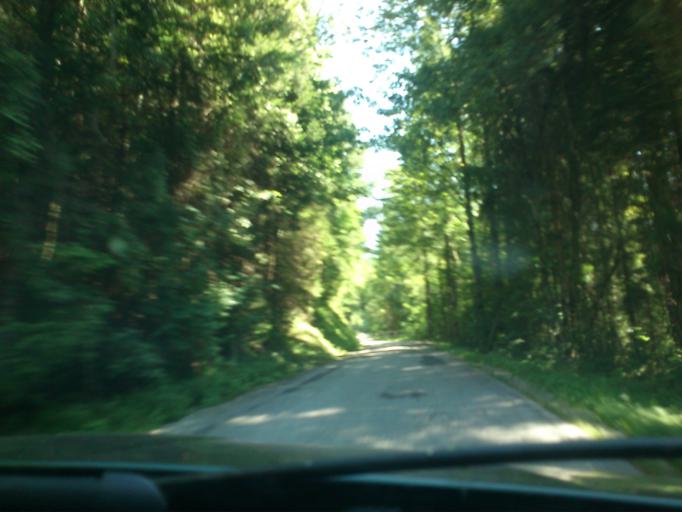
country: AT
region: Upper Austria
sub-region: Politischer Bezirk Kirchdorf an der Krems
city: Rossleithen
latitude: 47.7205
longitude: 14.3573
